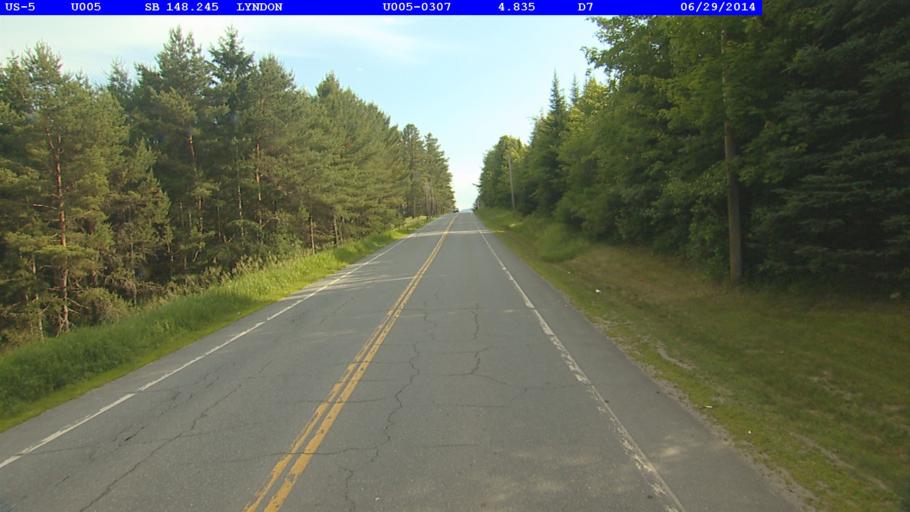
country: US
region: Vermont
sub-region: Caledonia County
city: Lyndonville
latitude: 44.5586
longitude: -71.9953
